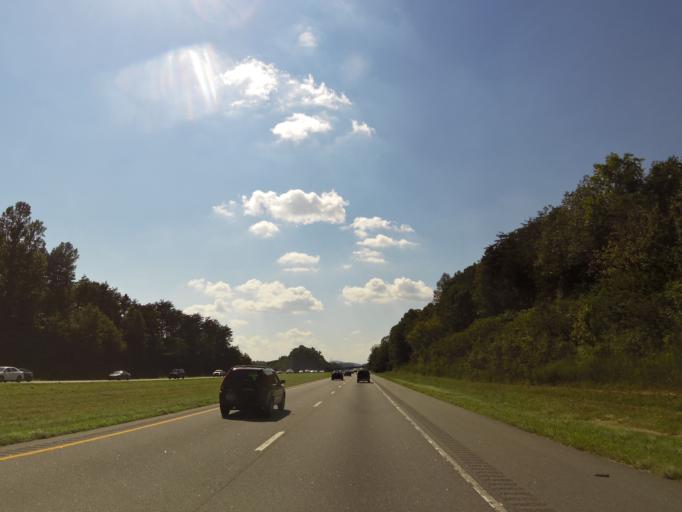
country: US
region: North Carolina
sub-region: Catawba County
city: Longview
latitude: 35.7066
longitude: -81.3818
